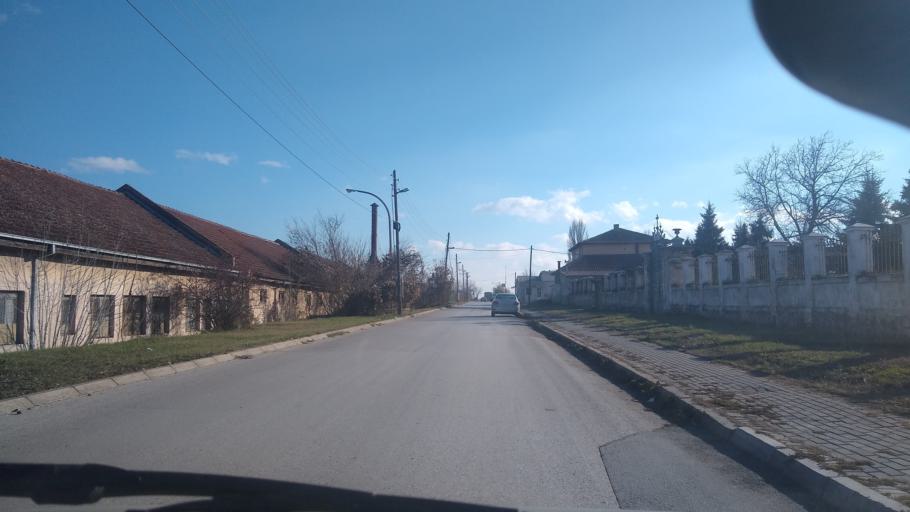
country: MK
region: Bitola
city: Bitola
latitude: 41.0144
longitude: 21.3452
